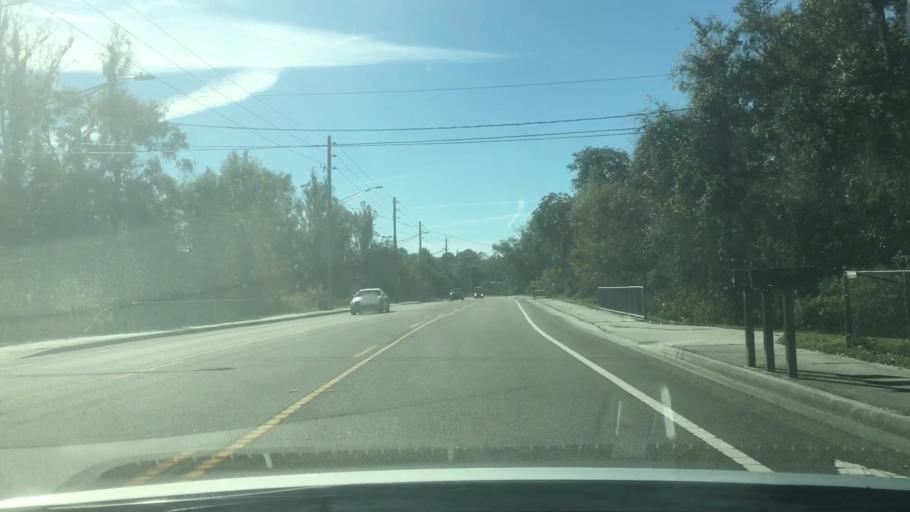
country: US
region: Florida
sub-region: Duval County
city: Jacksonville
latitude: 30.4706
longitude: -81.6157
